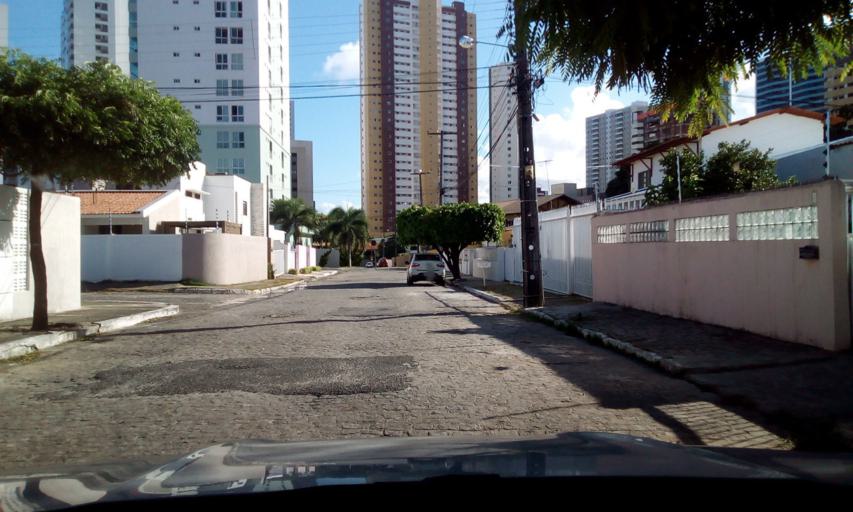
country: BR
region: Paraiba
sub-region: Joao Pessoa
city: Joao Pessoa
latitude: -7.1134
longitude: -34.8373
